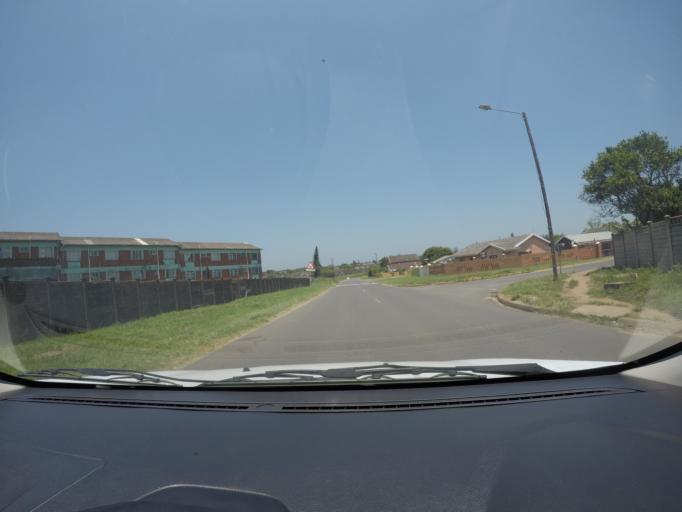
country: ZA
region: KwaZulu-Natal
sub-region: uThungulu District Municipality
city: eSikhawini
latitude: -28.8840
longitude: 31.8913
